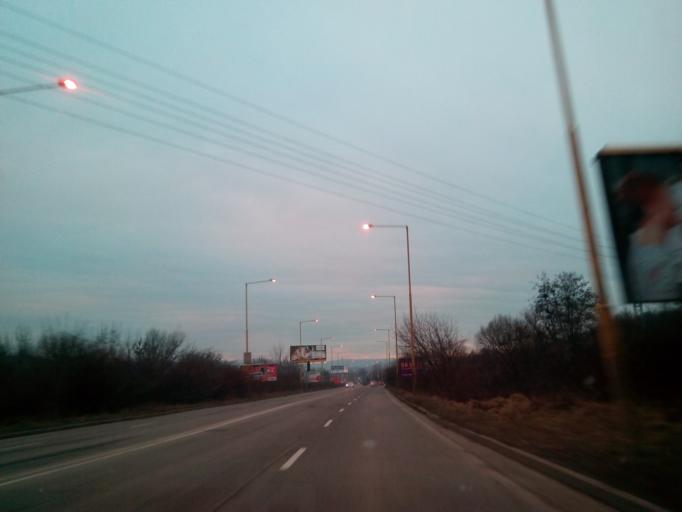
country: SK
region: Kosicky
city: Kosice
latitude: 48.6964
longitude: 21.2291
